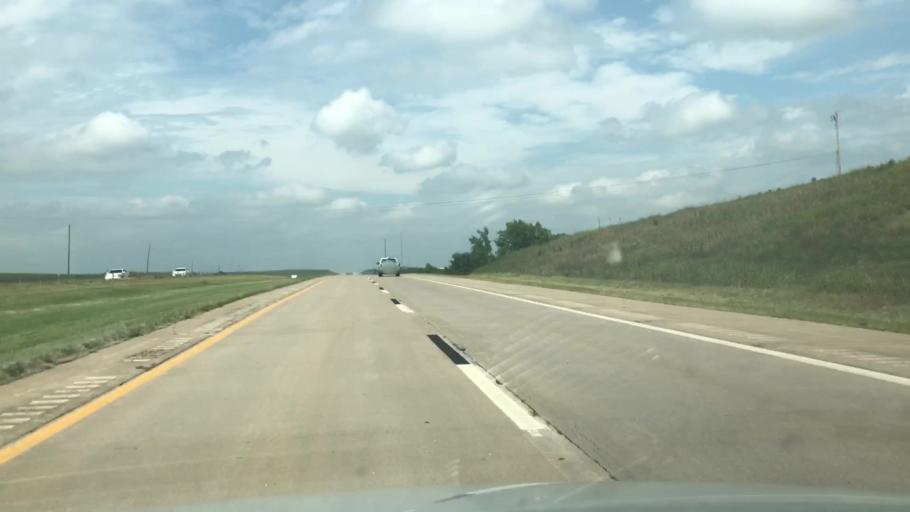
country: US
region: Oklahoma
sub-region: Osage County
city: Skiatook
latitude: 36.4780
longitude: -95.9204
